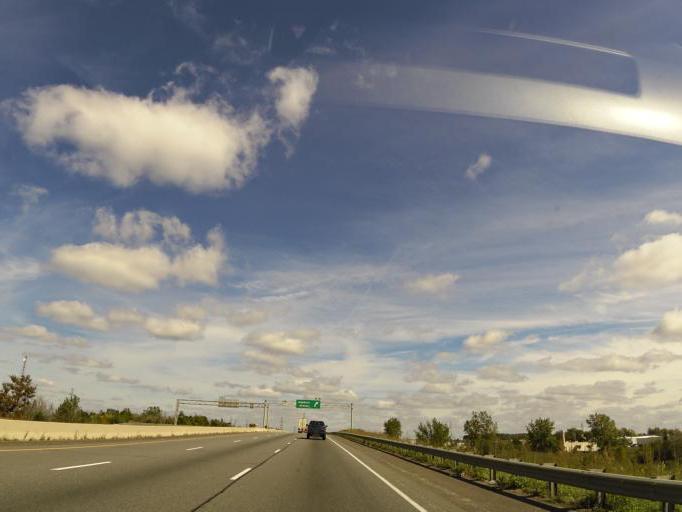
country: CA
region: Ontario
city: London
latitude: 42.9320
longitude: -81.1970
